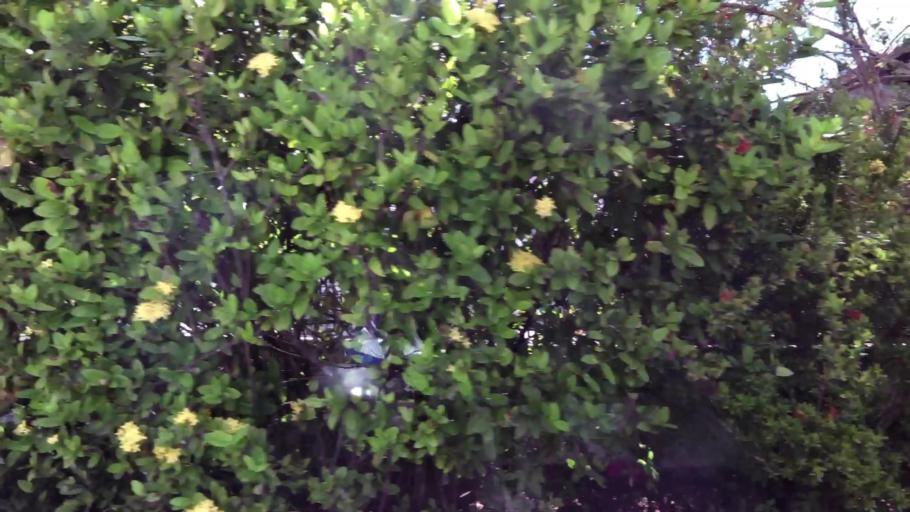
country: BN
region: Brunei and Muara
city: Bandar Seri Begawan
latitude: 4.9679
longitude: 114.9443
